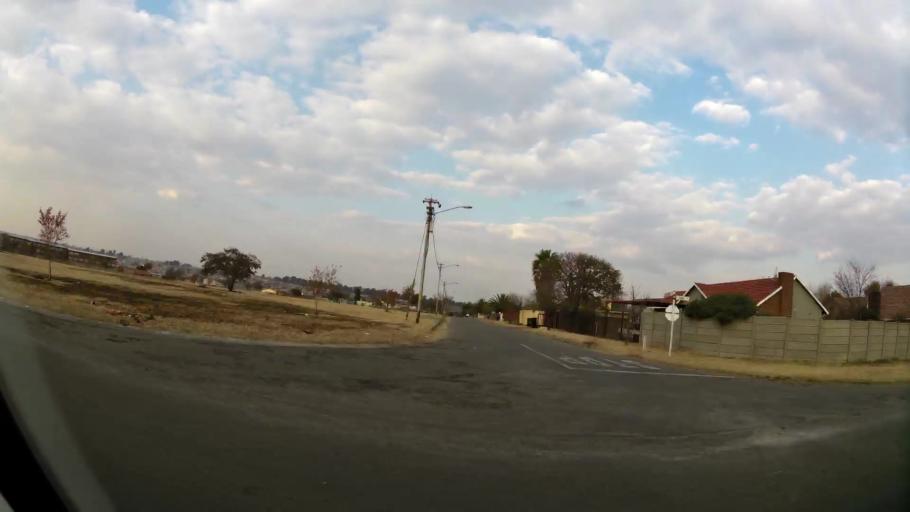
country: ZA
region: Gauteng
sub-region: Ekurhuleni Metropolitan Municipality
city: Germiston
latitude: -26.2388
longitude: 28.1969
